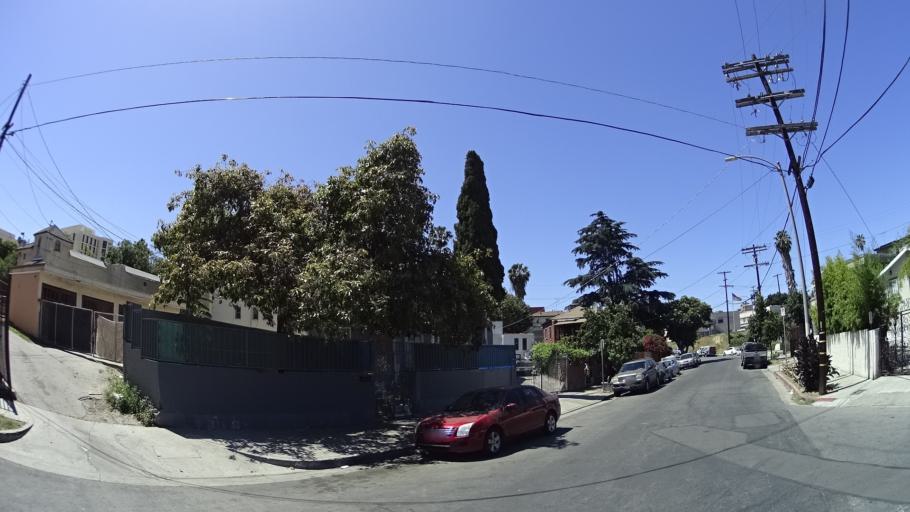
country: US
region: California
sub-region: Los Angeles County
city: Echo Park
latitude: 34.0658
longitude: -118.2750
